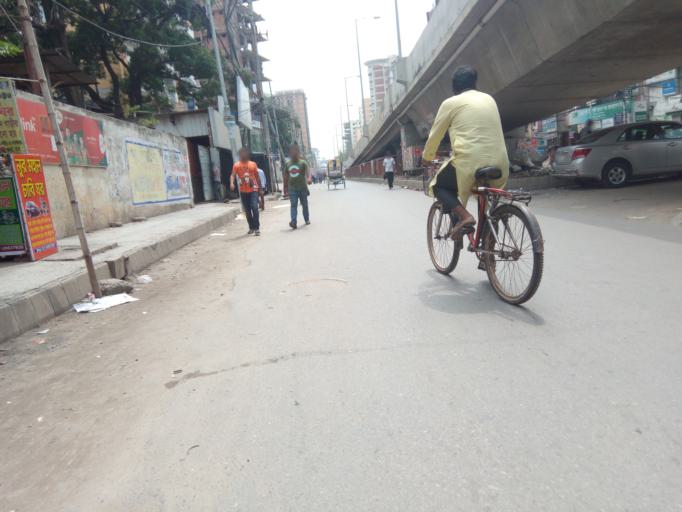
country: BD
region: Dhaka
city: Paltan
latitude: 23.7472
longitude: 90.3995
